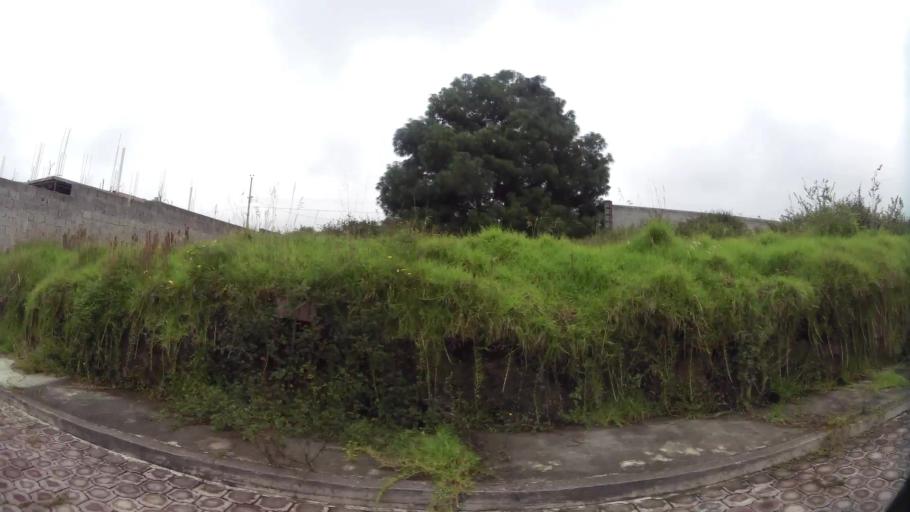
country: EC
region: Pichincha
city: Quito
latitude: -0.2678
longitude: -78.4732
